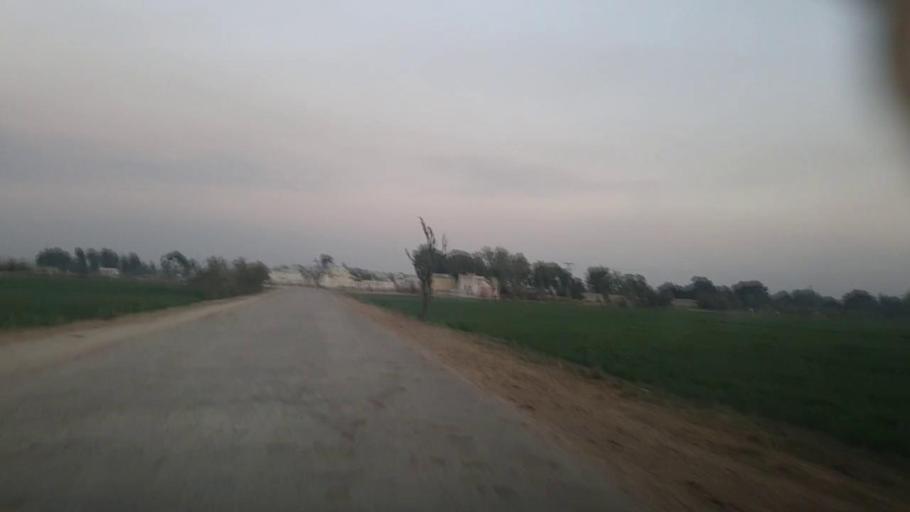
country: PK
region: Sindh
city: Kandiari
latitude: 26.6769
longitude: 68.9510
